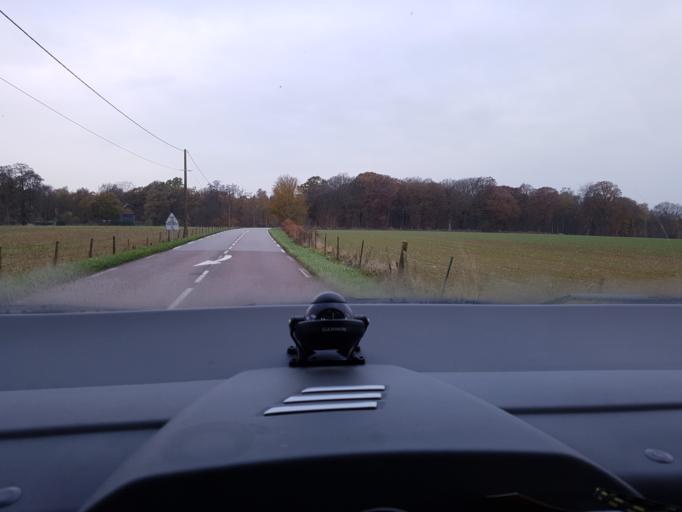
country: FR
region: Haute-Normandie
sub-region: Departement de la Seine-Maritime
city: Saint-Pierre-de-Varengeville
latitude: 49.4974
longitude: 0.9170
